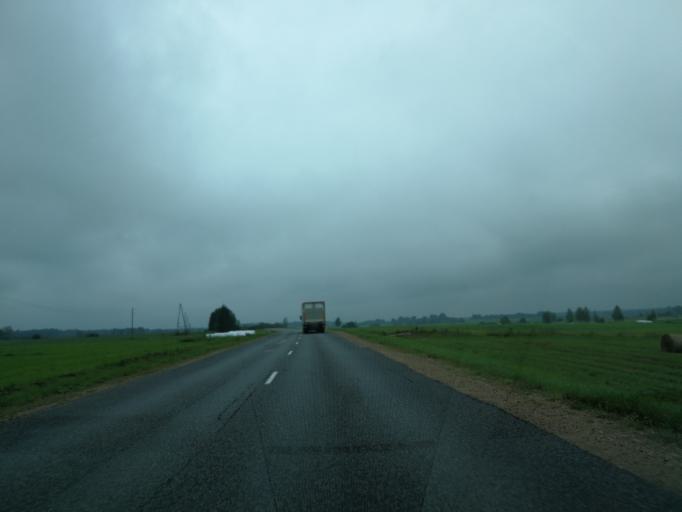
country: LV
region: Livani
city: Livani
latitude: 56.3533
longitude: 26.2477
